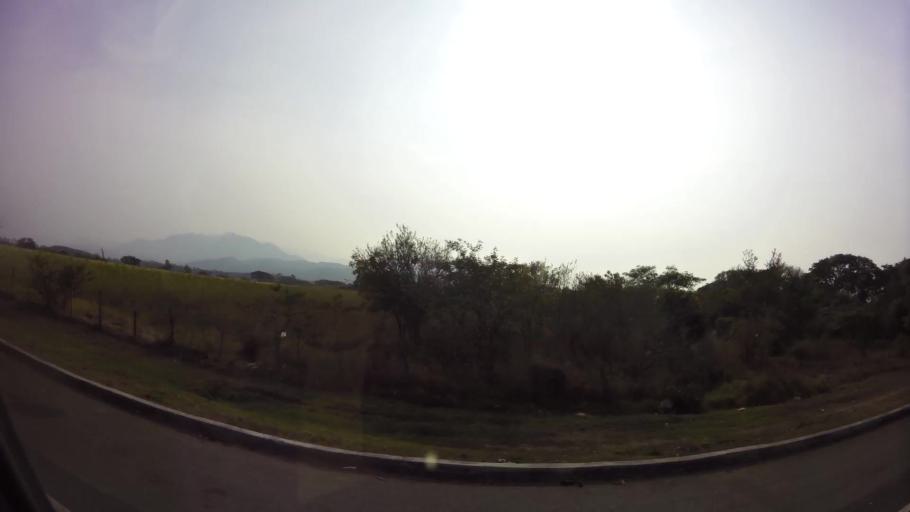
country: HN
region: La Paz
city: Yarumela
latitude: 14.3776
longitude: -87.6082
